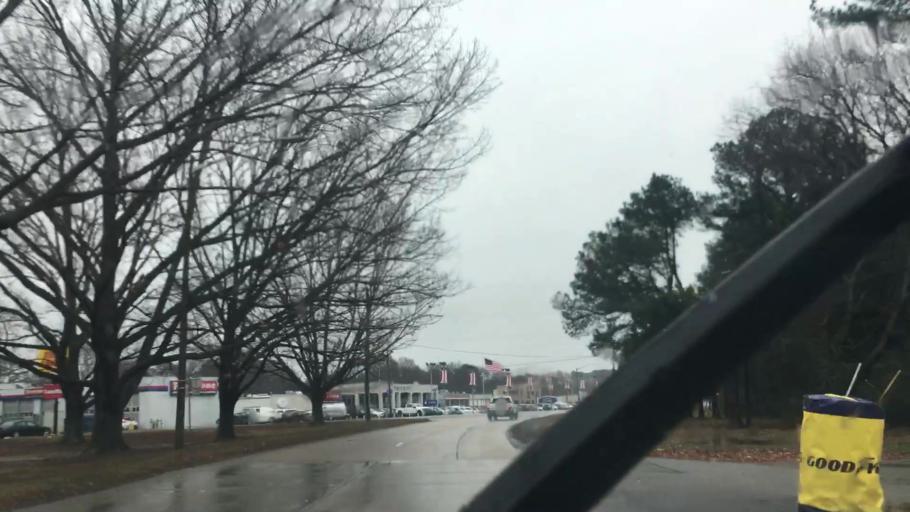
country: US
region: Virginia
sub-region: City of Norfolk
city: Norfolk
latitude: 36.9142
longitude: -76.2382
